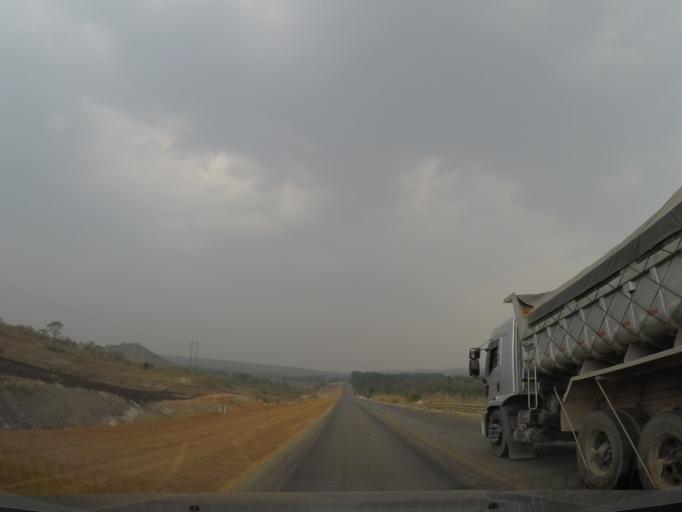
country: BR
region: Goias
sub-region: Pirenopolis
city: Pirenopolis
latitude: -15.8121
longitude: -48.7816
